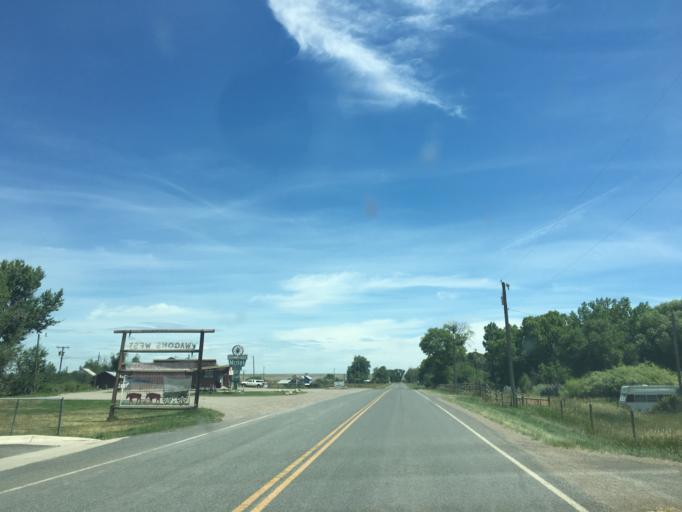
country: US
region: Montana
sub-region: Teton County
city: Choteau
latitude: 47.4951
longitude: -112.3884
